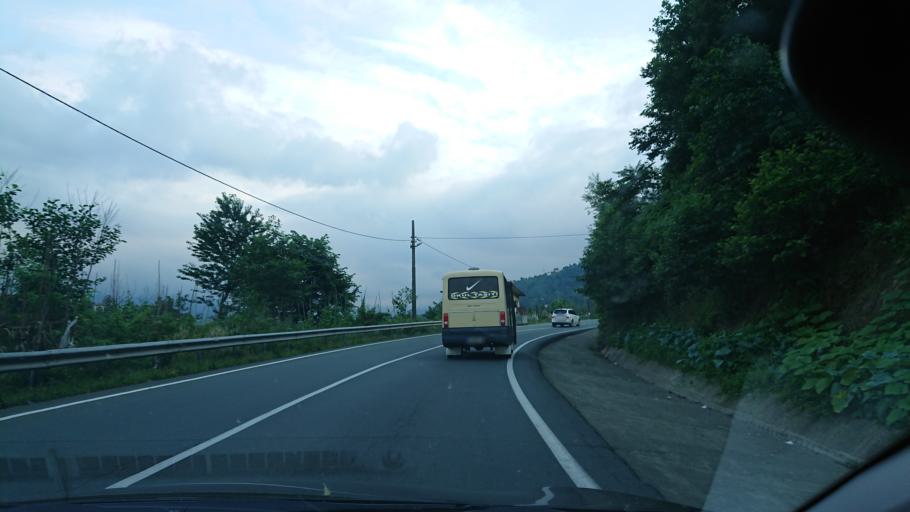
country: TR
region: Rize
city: Cayeli
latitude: 41.0783
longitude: 40.7135
